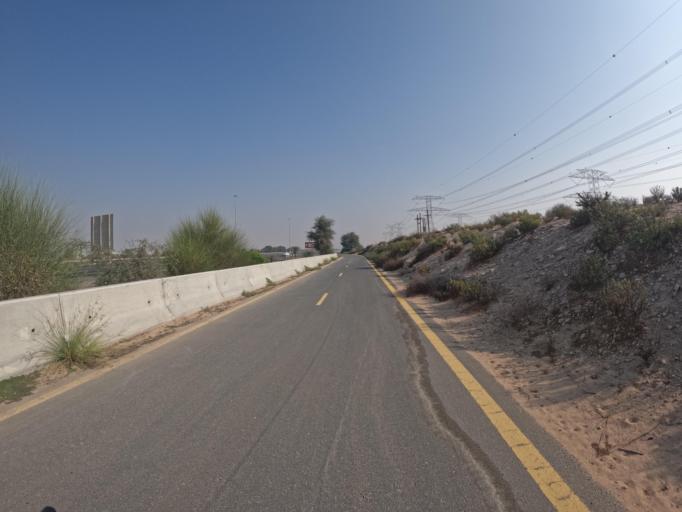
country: AE
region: Dubai
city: Dubai
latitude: 25.0409
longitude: 55.3042
